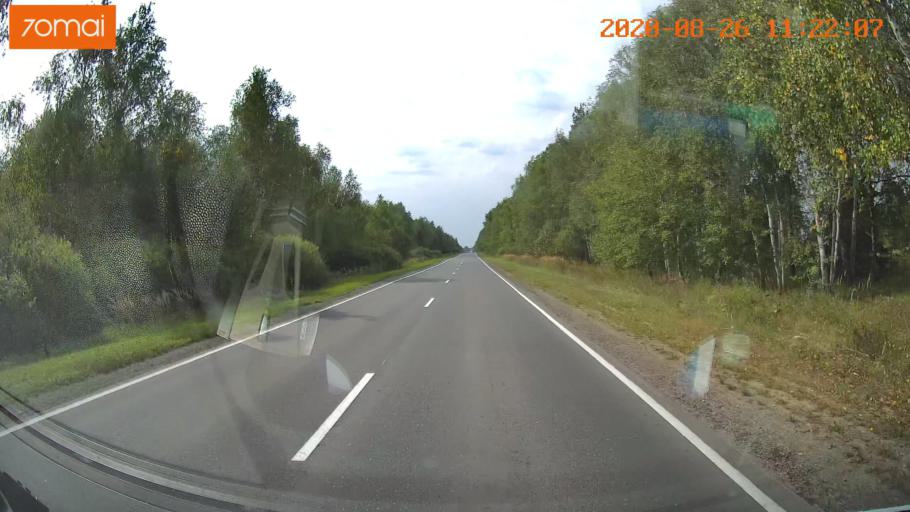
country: RU
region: Rjazan
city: Shilovo
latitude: 54.3679
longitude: 41.0329
